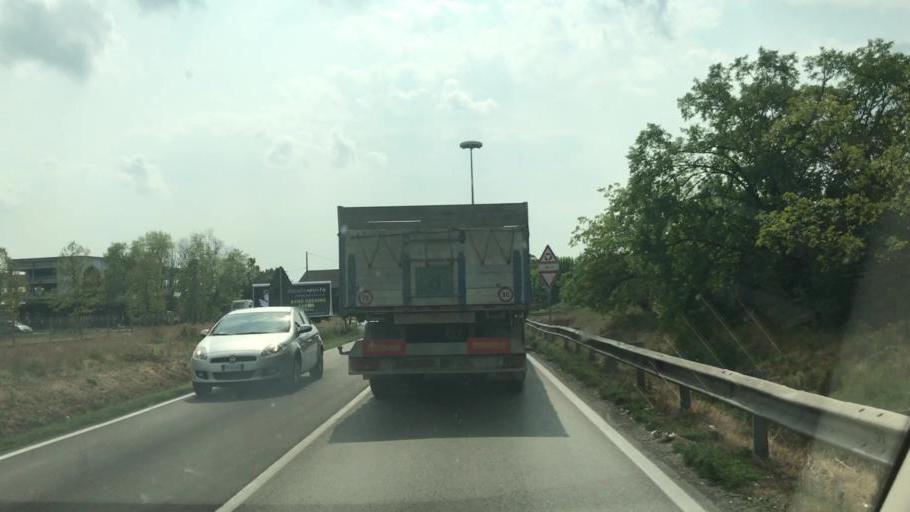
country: IT
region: Emilia-Romagna
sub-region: Provincia di Parma
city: Baganzola
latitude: 44.8491
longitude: 10.3414
